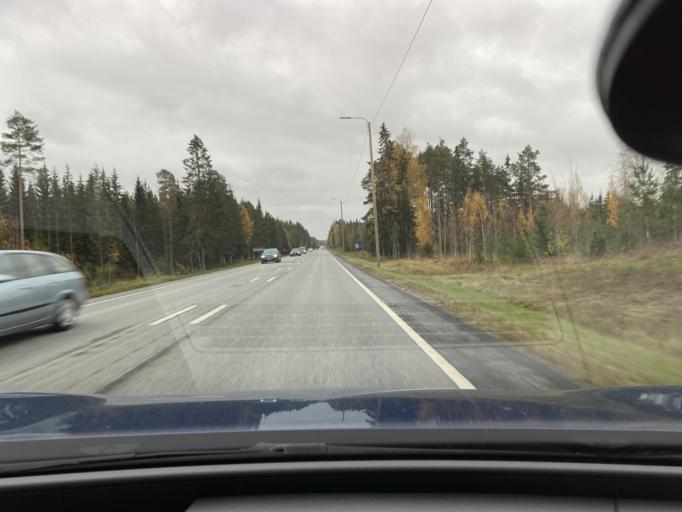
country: FI
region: Varsinais-Suomi
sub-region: Vakka-Suomi
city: Laitila
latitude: 60.9531
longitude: 21.5975
